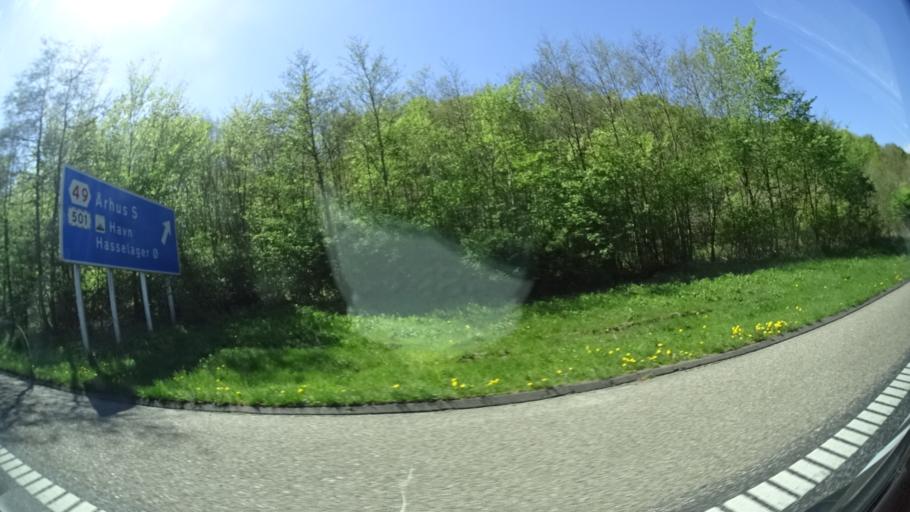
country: DK
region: Central Jutland
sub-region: Skanderborg Kommune
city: Horning
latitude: 56.1241
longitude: 10.0349
